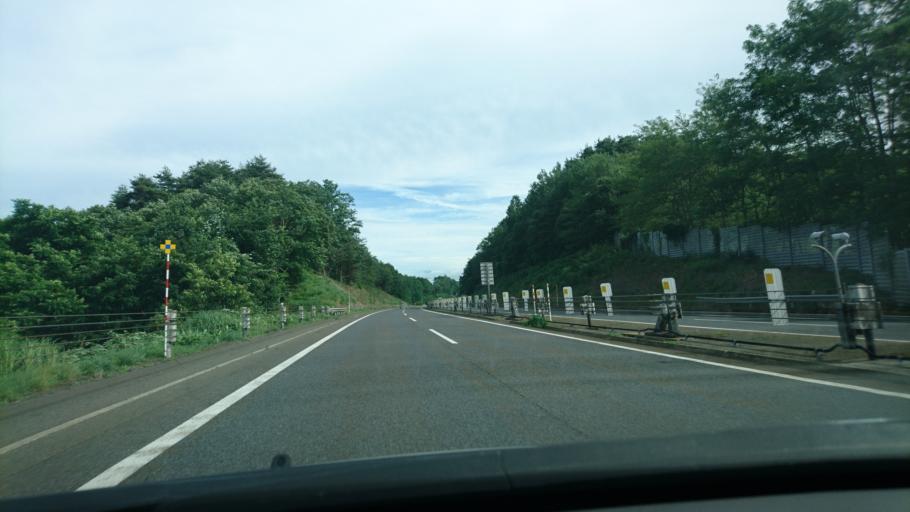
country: JP
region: Iwate
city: Shizukuishi
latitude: 39.9659
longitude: 141.0297
